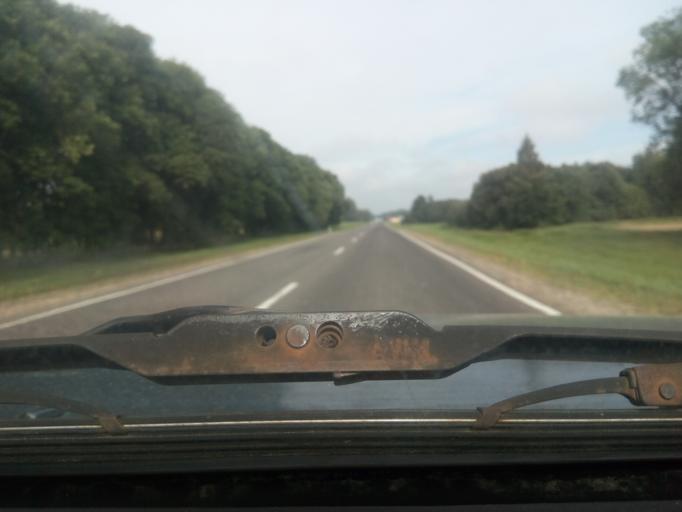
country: BY
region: Vitebsk
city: Vyerkhnyadzvinsk
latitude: 55.7371
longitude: 27.9914
